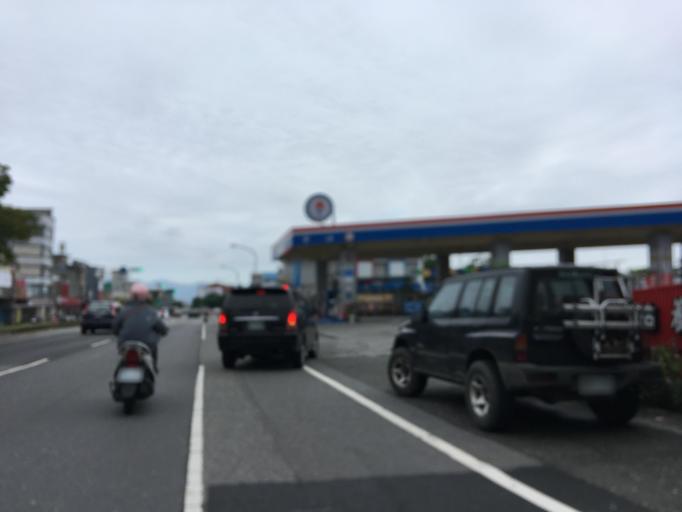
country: TW
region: Taiwan
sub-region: Yilan
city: Yilan
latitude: 24.6972
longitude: 121.7692
